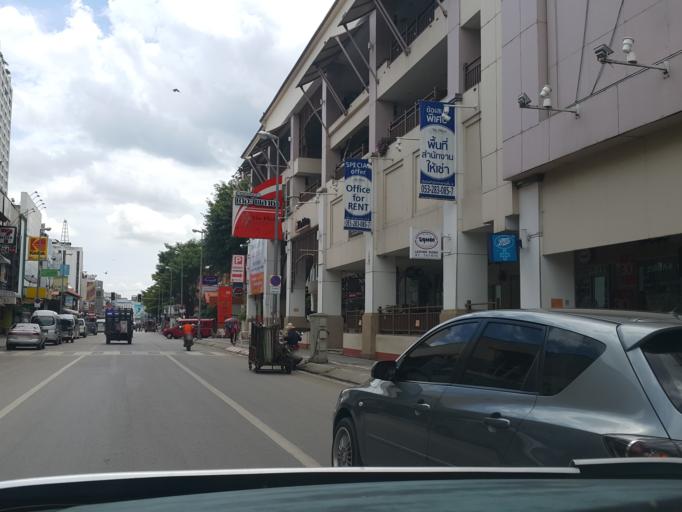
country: TH
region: Chiang Mai
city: Chiang Mai
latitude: 18.7863
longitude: 99.0008
